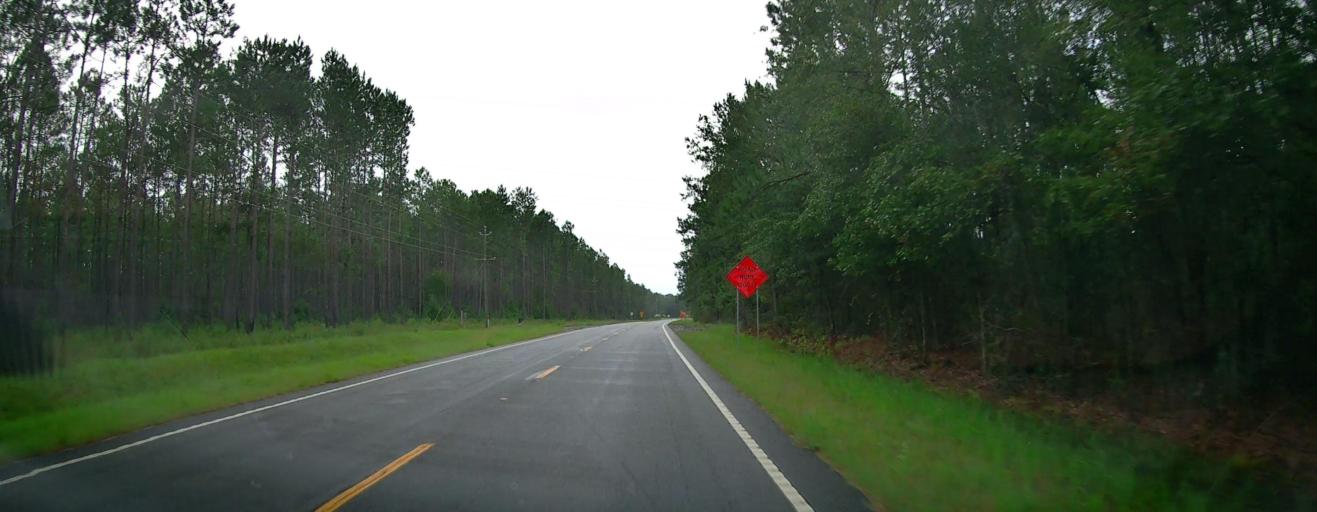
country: US
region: Georgia
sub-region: Ware County
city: Deenwood
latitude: 31.2671
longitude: -82.5211
